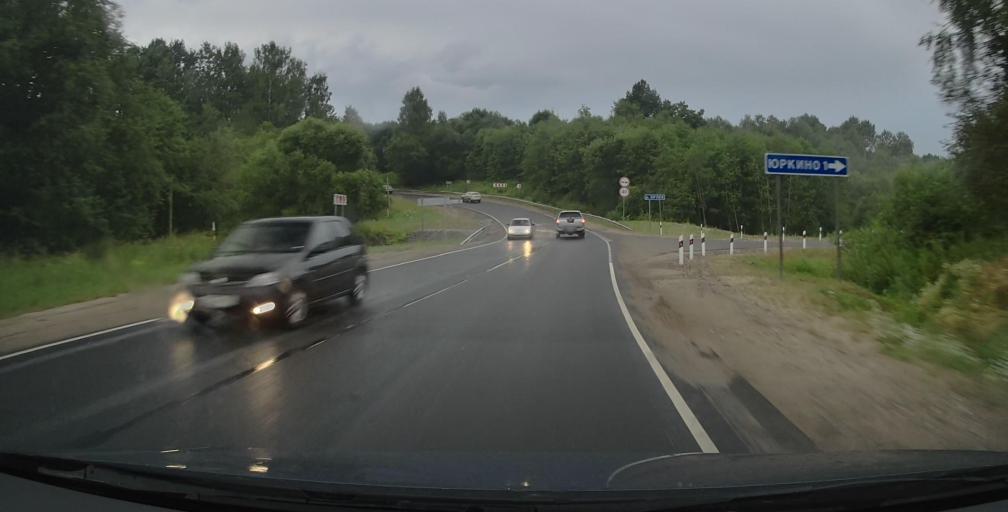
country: RU
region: Jaroslavl
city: Uglich
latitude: 57.5577
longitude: 38.2765
